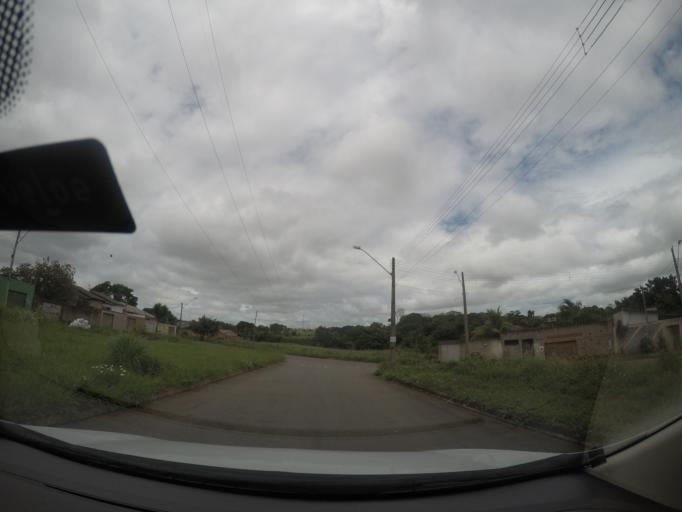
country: BR
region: Goias
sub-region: Goiania
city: Goiania
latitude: -16.7400
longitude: -49.3725
